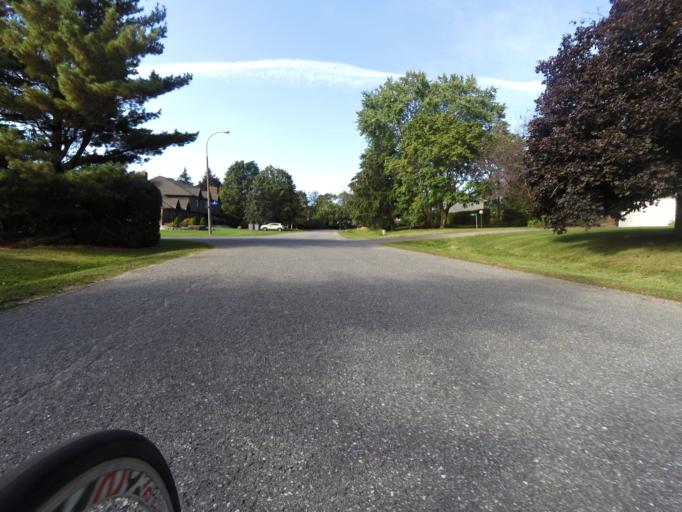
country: CA
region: Ontario
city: Bells Corners
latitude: 45.2681
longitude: -75.7172
